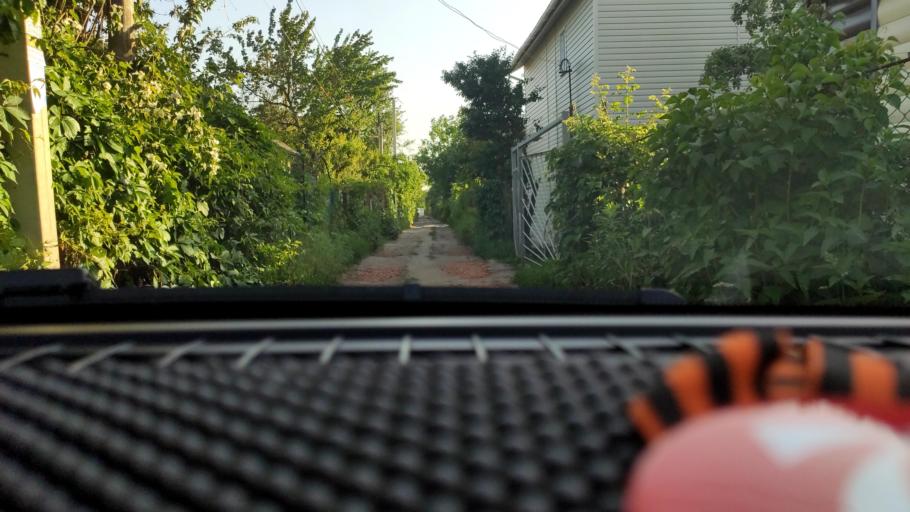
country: RU
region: Voronezj
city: Maslovka
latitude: 51.5918
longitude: 39.1619
